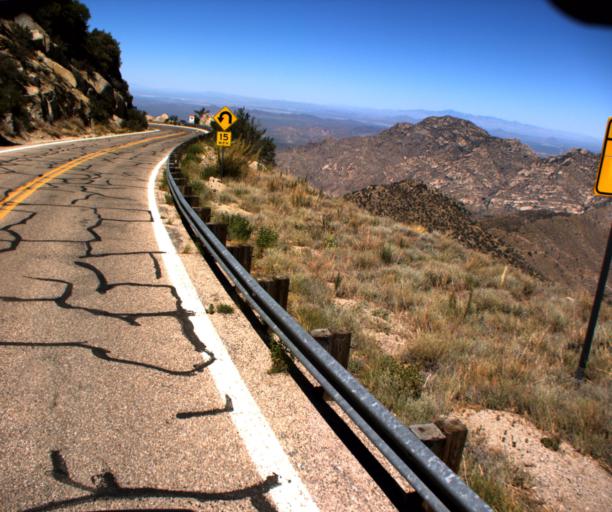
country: US
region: Arizona
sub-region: Pima County
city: Sells
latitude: 31.9645
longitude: -111.5987
